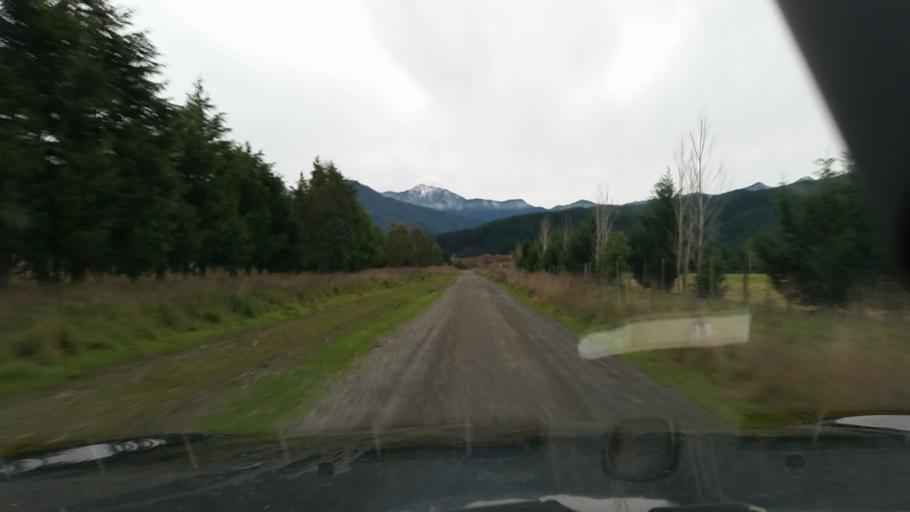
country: NZ
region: Marlborough
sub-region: Marlborough District
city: Blenheim
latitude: -41.5354
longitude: 173.6136
